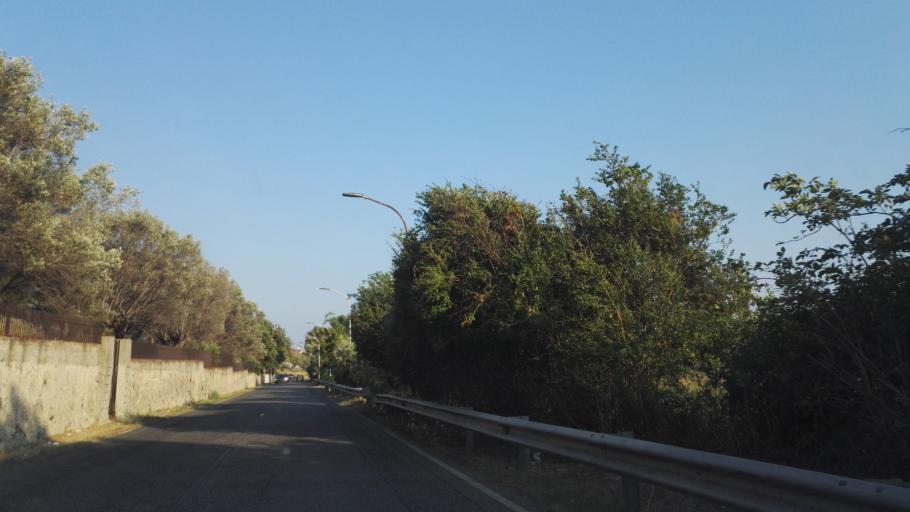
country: IT
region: Calabria
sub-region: Provincia di Reggio Calabria
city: Marina di Gioiosa Ionica
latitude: 38.3080
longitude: 16.3194
